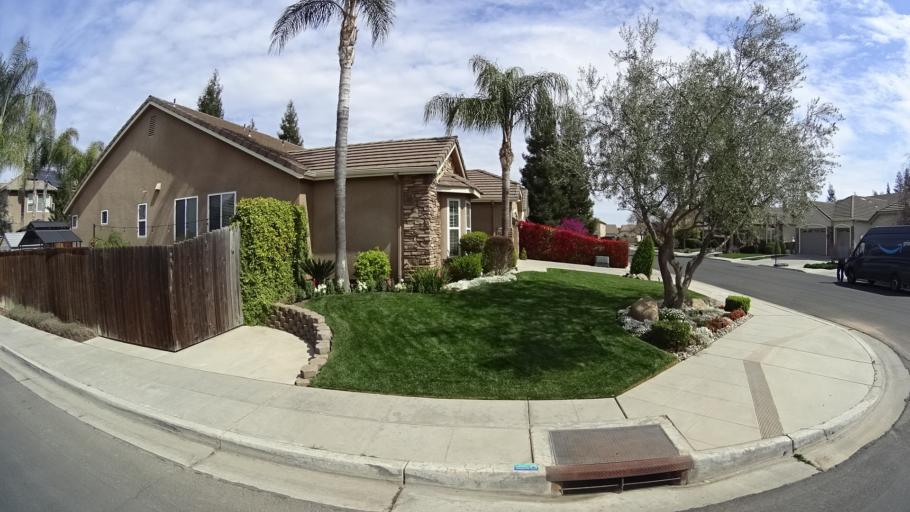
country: US
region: California
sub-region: Fresno County
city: Biola
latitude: 36.8413
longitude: -119.8968
